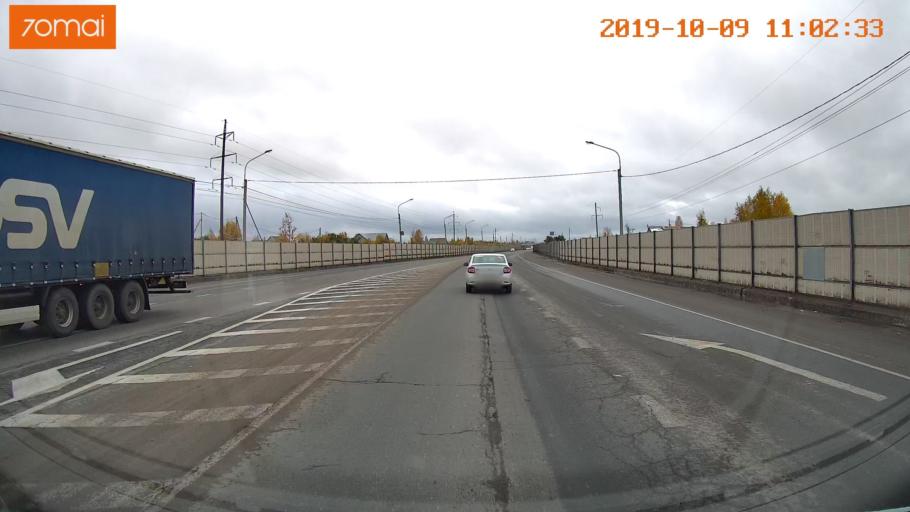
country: RU
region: Vologda
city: Vologda
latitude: 59.2310
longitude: 39.7746
